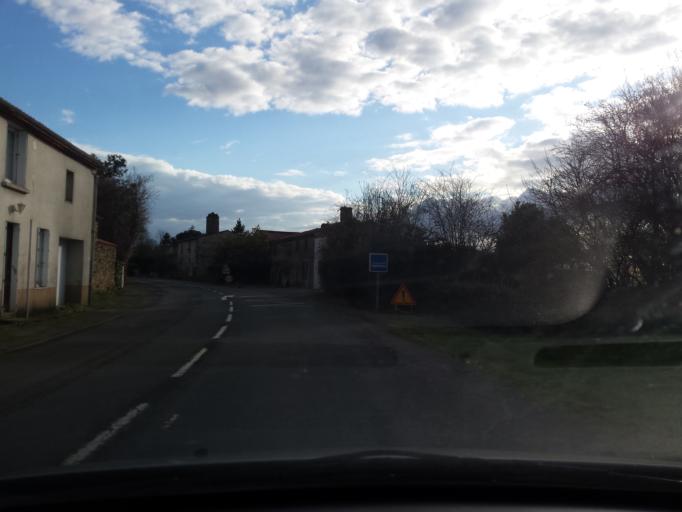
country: FR
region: Pays de la Loire
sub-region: Departement de la Vendee
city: Saint-Martin-des-Noyers
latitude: 46.7152
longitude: -1.2104
